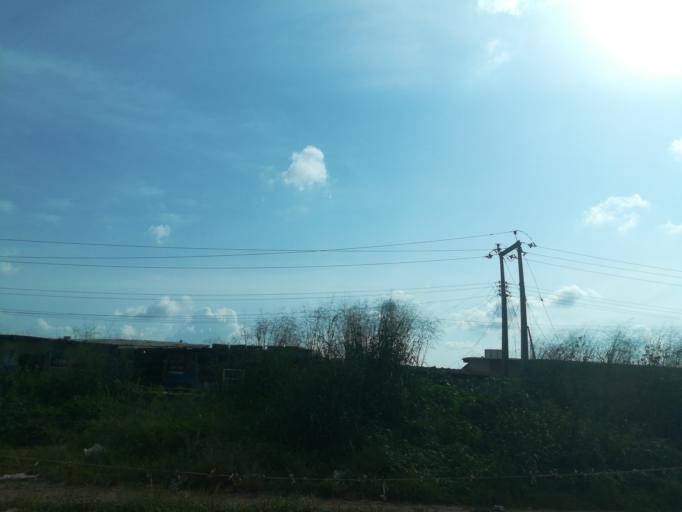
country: NG
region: Oyo
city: Ibadan
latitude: 7.3903
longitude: 3.8193
